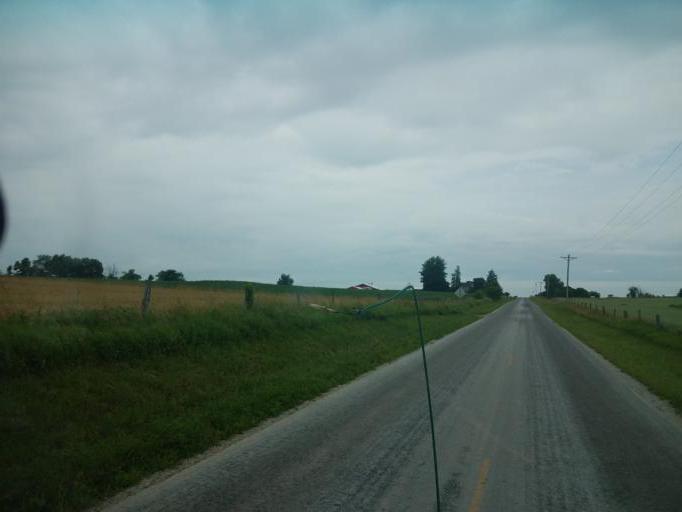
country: US
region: Ohio
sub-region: Hardin County
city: Kenton
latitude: 40.6300
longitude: -83.5382
